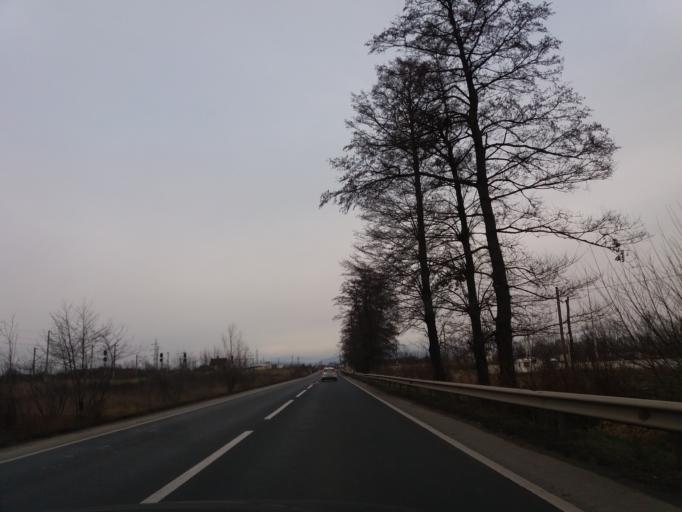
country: RO
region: Hunedoara
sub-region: Comuna Bacia
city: Bacia
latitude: 45.7926
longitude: 23.0013
